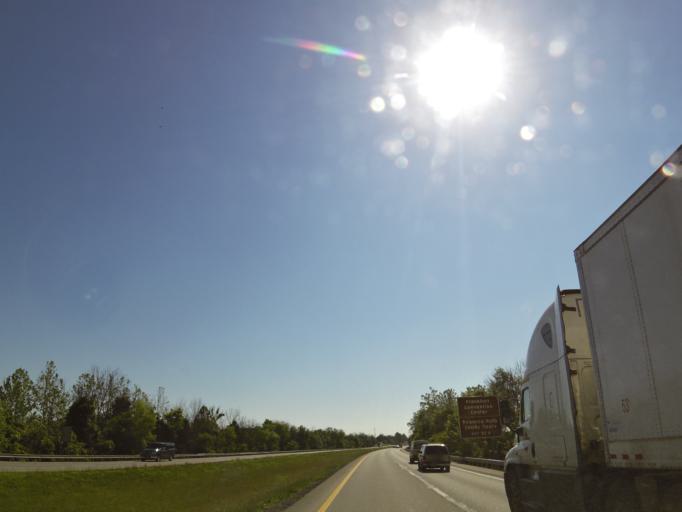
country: US
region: Kentucky
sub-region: Franklin County
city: Frankfort
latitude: 38.1582
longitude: -84.9125
